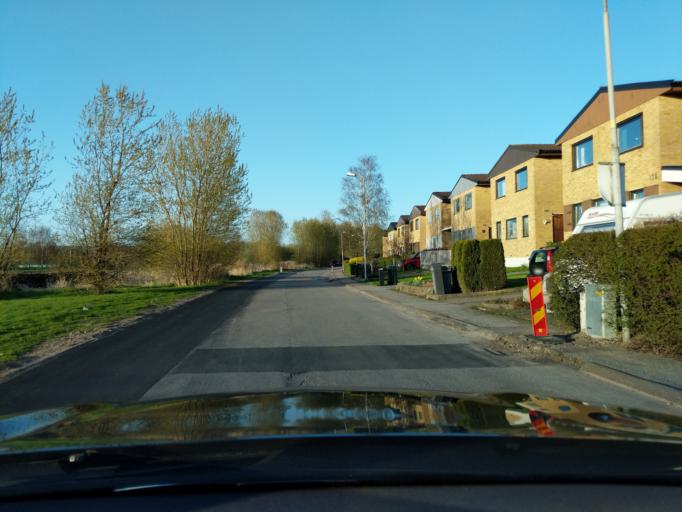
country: SE
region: Vaestra Goetaland
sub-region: Goteborg
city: Majorna
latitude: 57.6404
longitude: 11.9261
